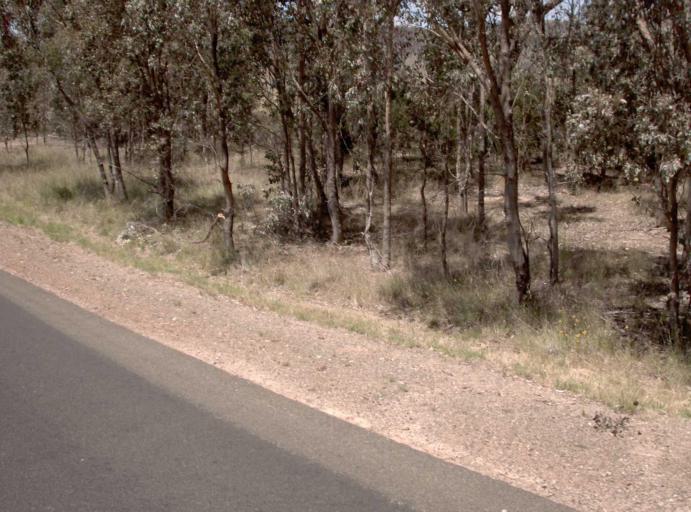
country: AU
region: Victoria
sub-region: East Gippsland
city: Bairnsdale
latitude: -37.1674
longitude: 147.6887
